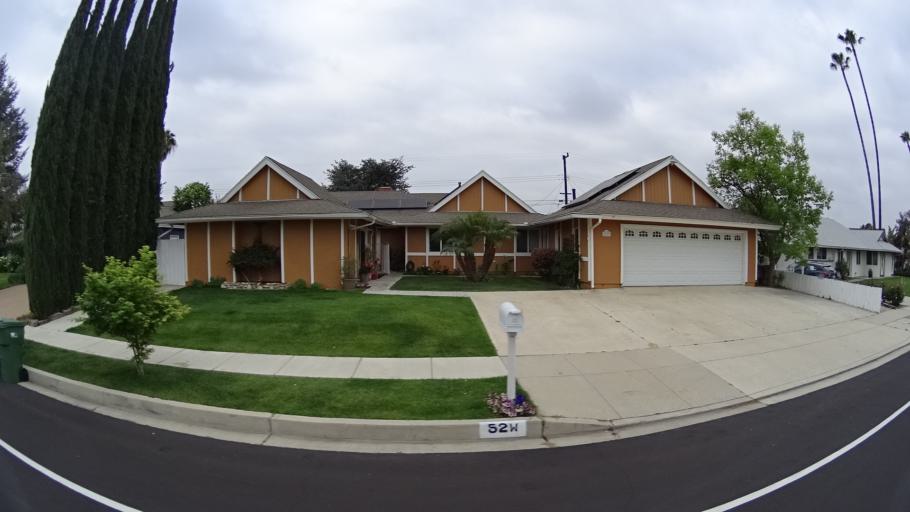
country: US
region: California
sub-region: Ventura County
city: Thousand Oaks
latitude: 34.2119
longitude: -118.8761
